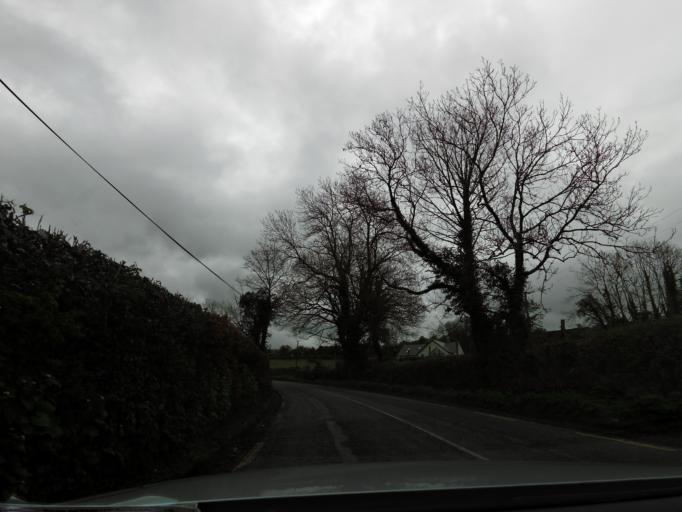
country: IE
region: Leinster
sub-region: Kilkenny
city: Kilkenny
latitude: 52.7034
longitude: -7.3097
